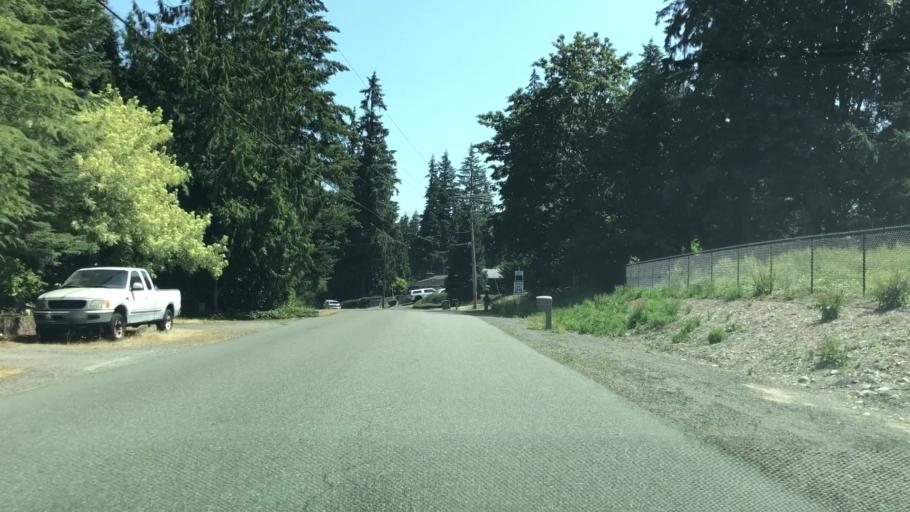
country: US
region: Washington
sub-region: King County
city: Cottage Lake
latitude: 47.7437
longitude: -122.1022
